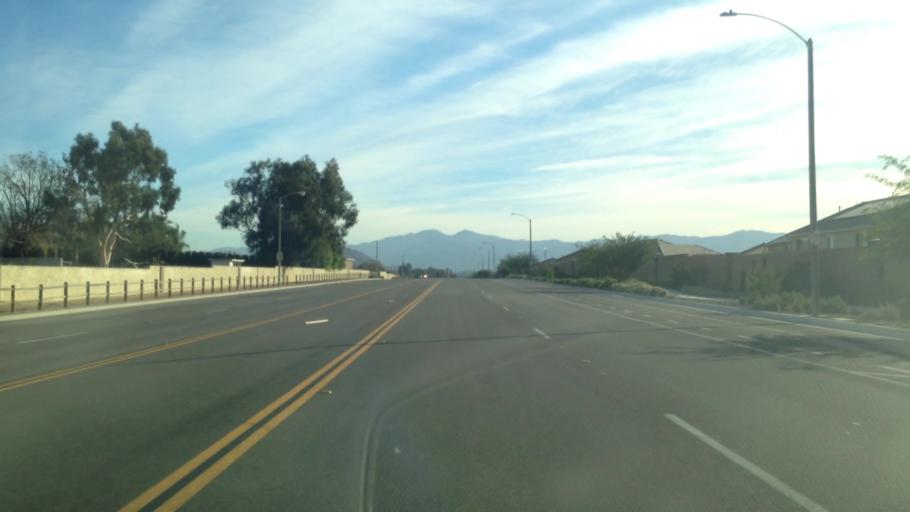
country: US
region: California
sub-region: Riverside County
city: Mira Loma
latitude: 33.9829
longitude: -117.5406
